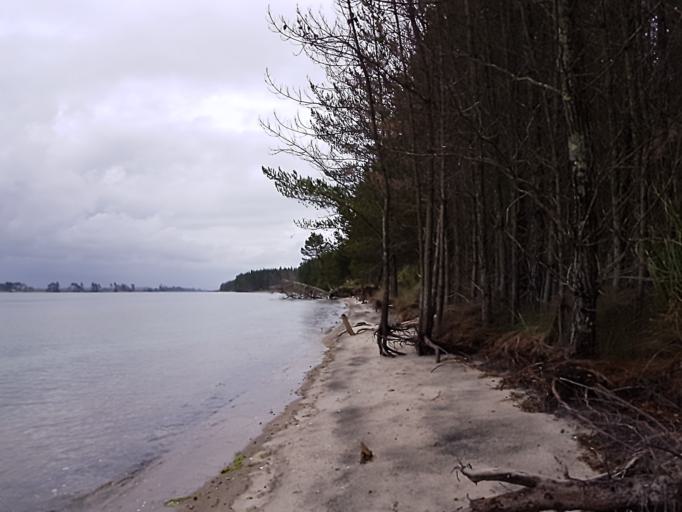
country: NZ
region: Bay of Plenty
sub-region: Tauranga City
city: Tauranga
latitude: -37.6369
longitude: 176.1412
